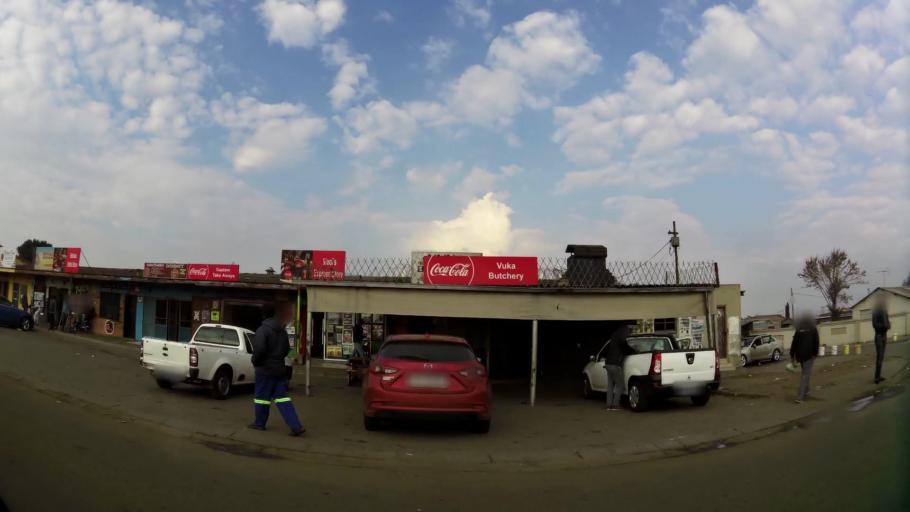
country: ZA
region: Gauteng
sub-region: Sedibeng District Municipality
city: Vanderbijlpark
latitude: -26.6939
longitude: 27.8663
